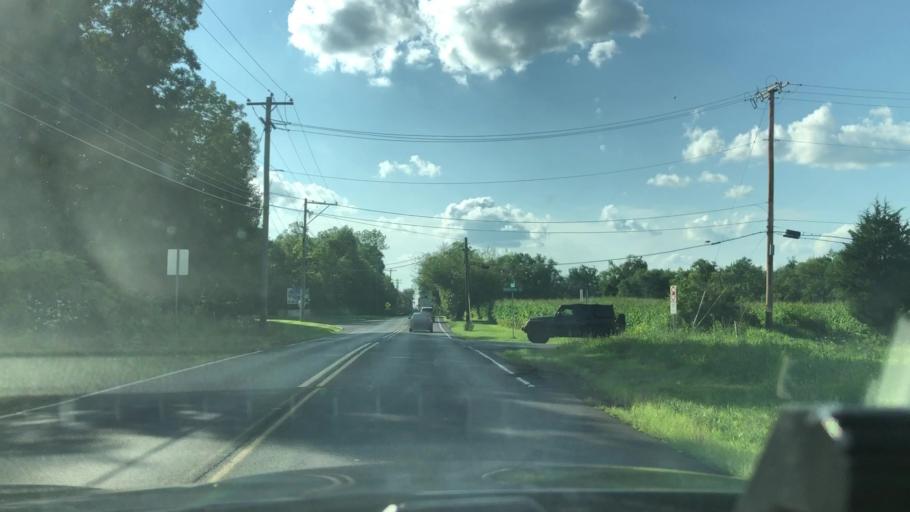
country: US
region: Pennsylvania
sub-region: Montgomery County
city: Montgomeryville
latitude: 40.2804
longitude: -75.2537
